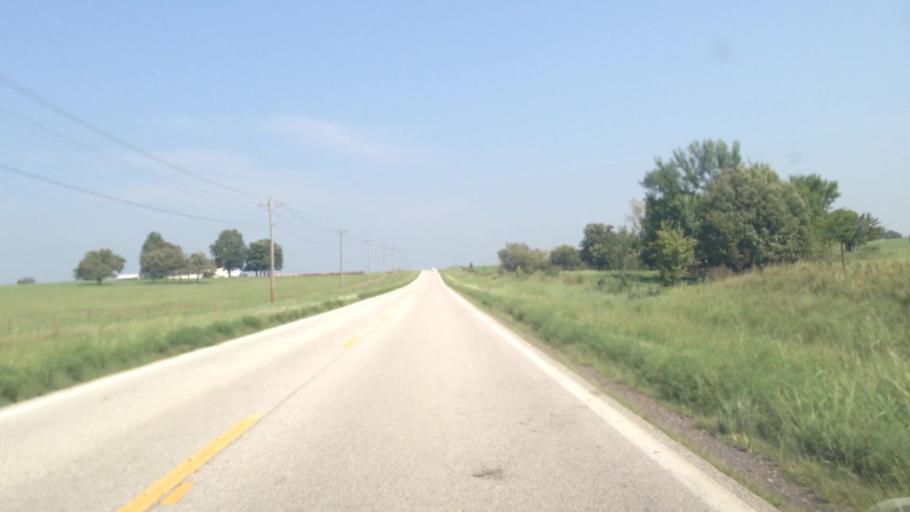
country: US
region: Oklahoma
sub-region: Craig County
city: Vinita
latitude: 36.7356
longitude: -95.1436
